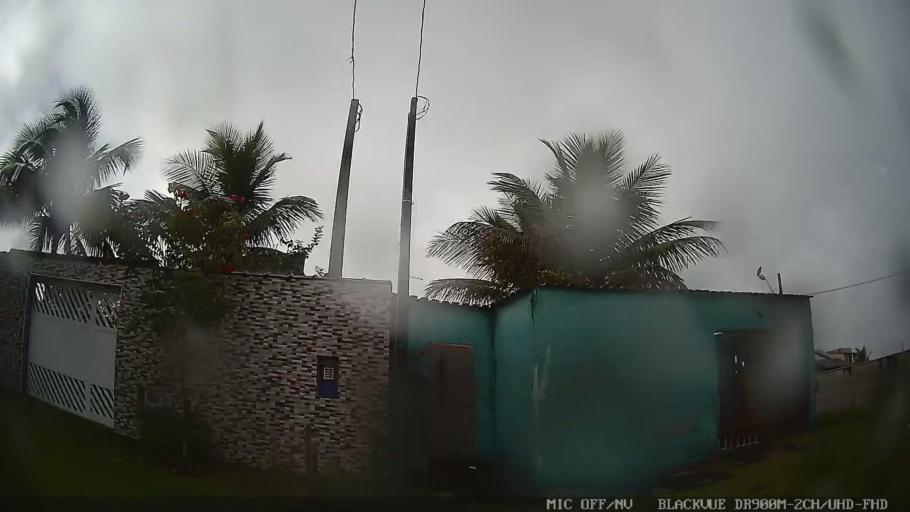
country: BR
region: Sao Paulo
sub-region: Peruibe
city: Peruibe
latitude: -24.2487
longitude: -46.8991
